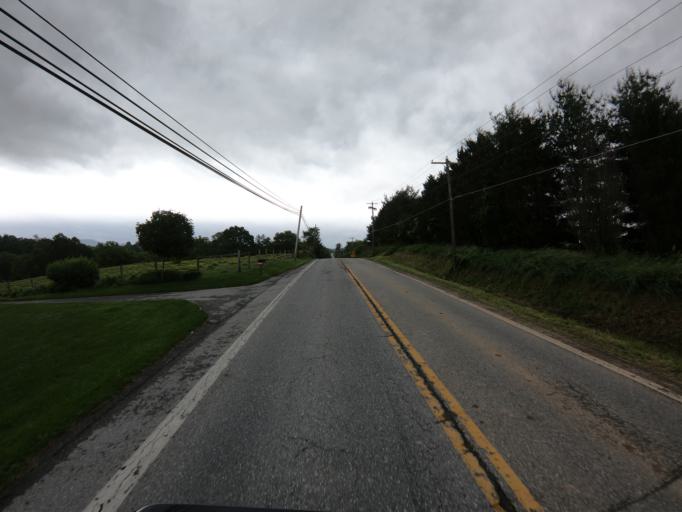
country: US
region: Maryland
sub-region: Frederick County
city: Middletown
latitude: 39.4524
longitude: -77.5666
